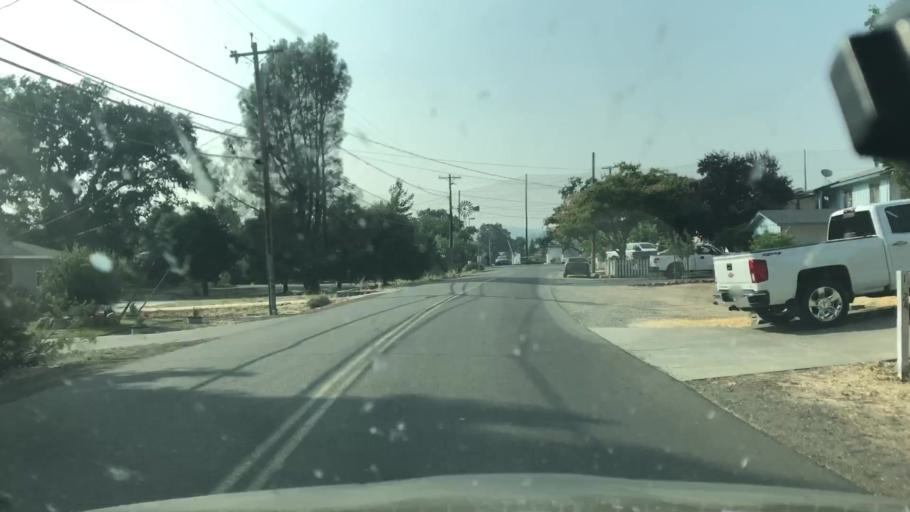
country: US
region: California
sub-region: Lake County
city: Hidden Valley Lake
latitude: 38.7955
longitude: -122.5533
